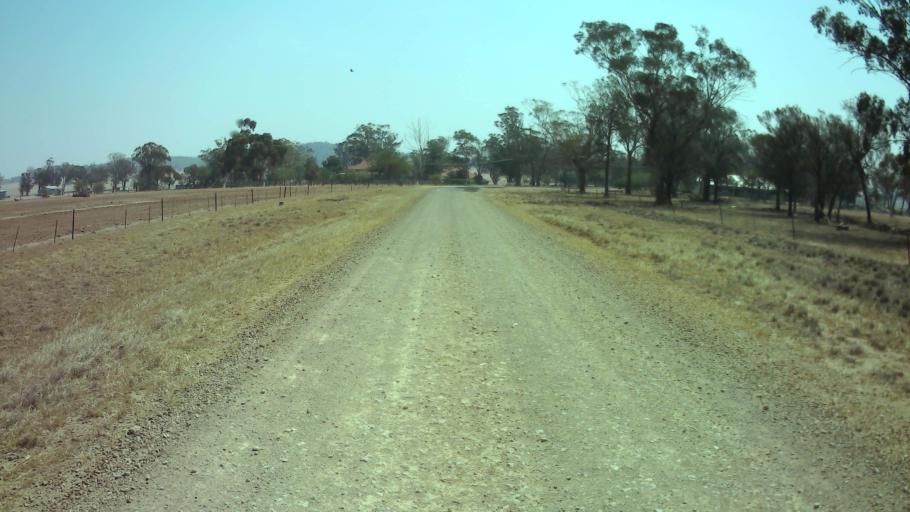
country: AU
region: New South Wales
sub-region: Weddin
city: Grenfell
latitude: -33.6430
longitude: 148.2554
